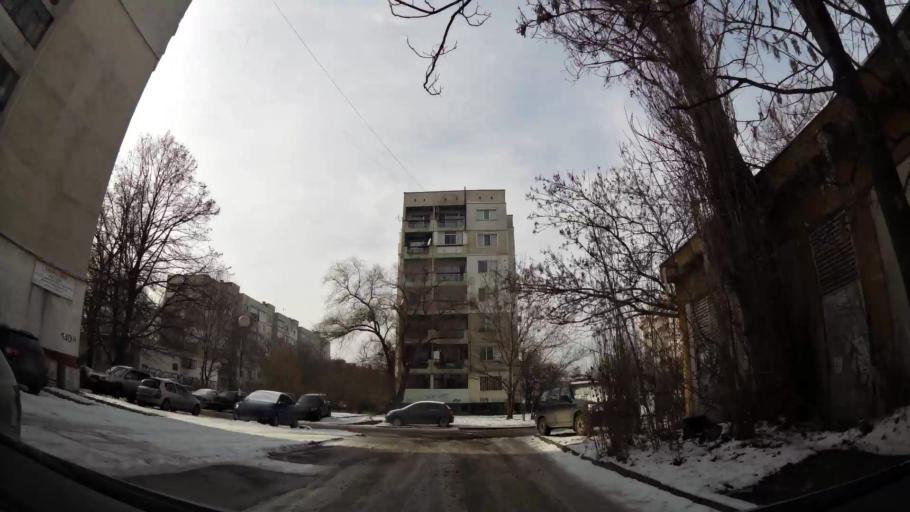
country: BG
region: Sofia-Capital
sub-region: Stolichna Obshtina
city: Sofia
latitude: 42.7060
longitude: 23.3560
